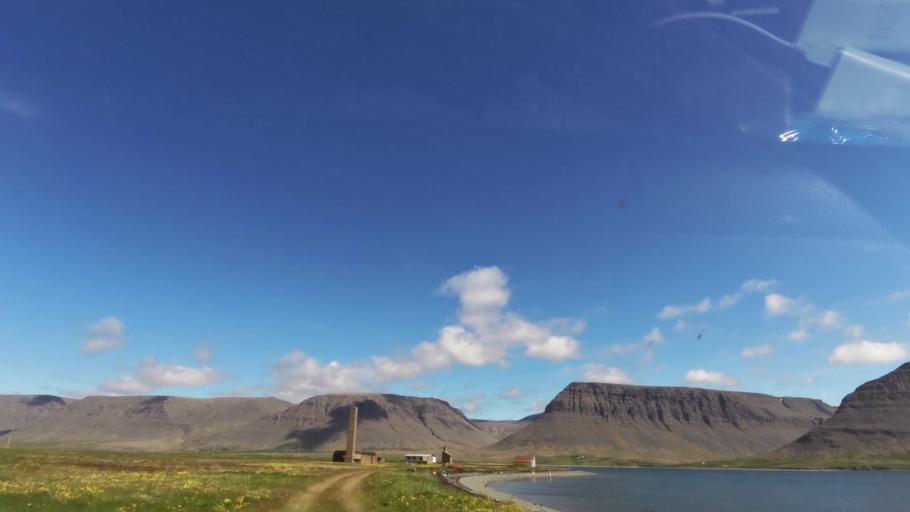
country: IS
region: West
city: Olafsvik
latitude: 65.6378
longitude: -23.9324
